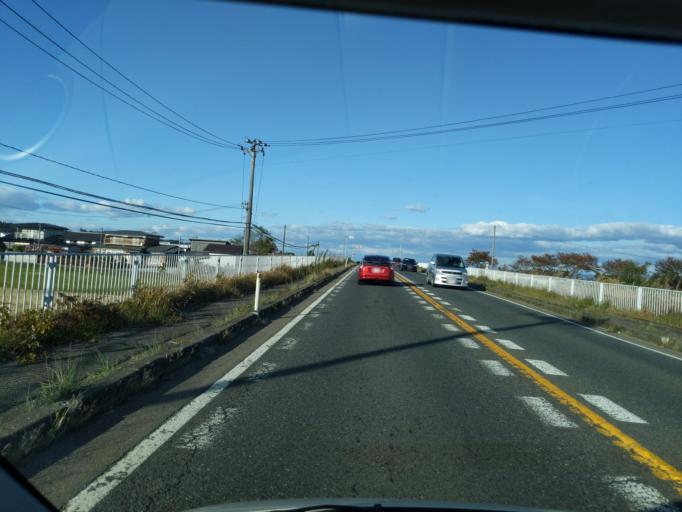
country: JP
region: Iwate
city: Mizusawa
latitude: 39.0564
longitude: 141.1344
